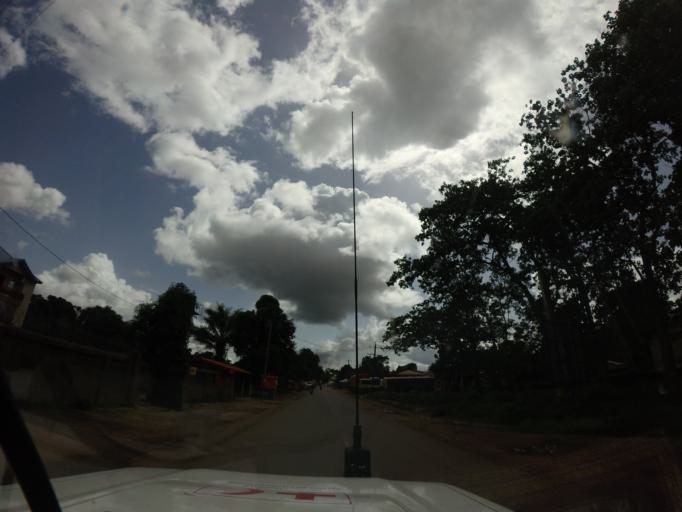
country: GN
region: Mamou
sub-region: Mamou Prefecture
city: Mamou
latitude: 10.3715
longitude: -12.0734
